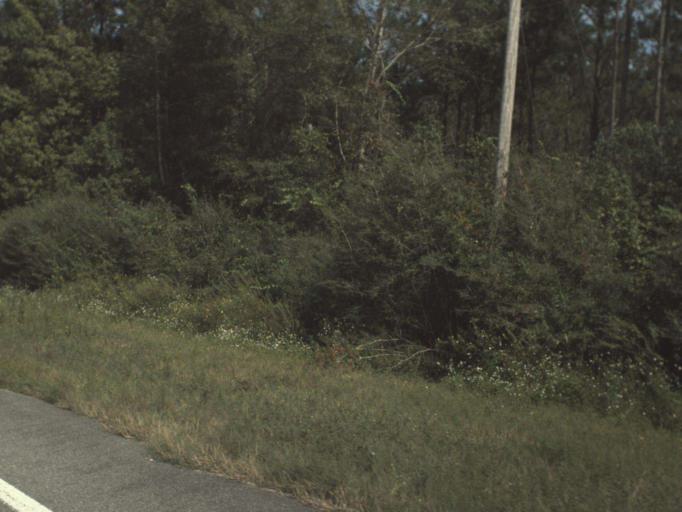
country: US
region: Florida
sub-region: Washington County
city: Chipley
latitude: 30.5966
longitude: -85.5941
